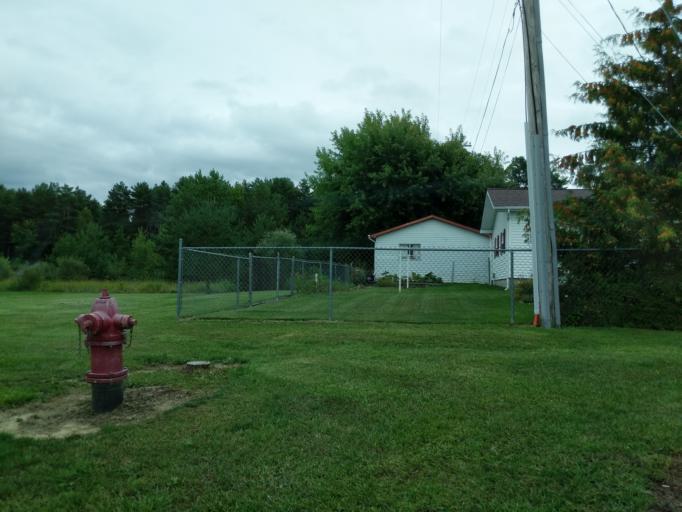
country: US
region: Michigan
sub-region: Tuscola County
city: Caro
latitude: 43.3371
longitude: -83.3597
